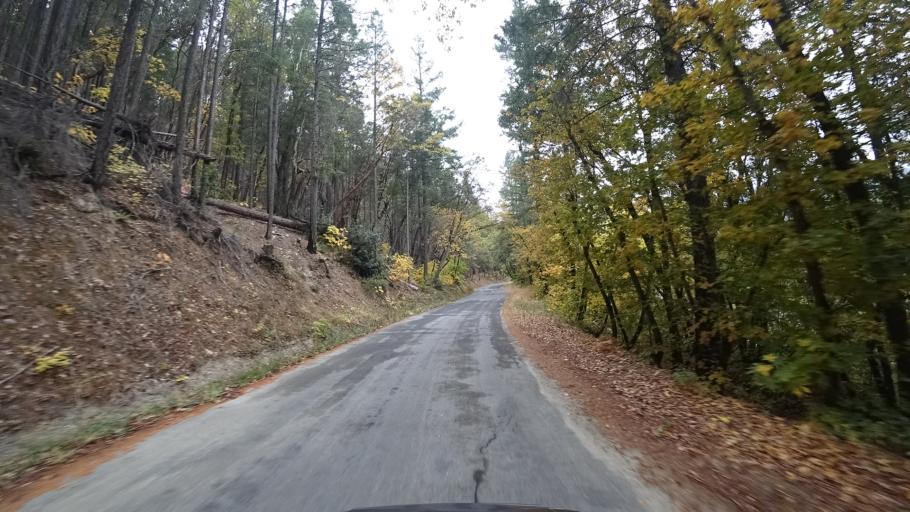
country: US
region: California
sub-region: Siskiyou County
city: Happy Camp
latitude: 41.8257
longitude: -123.1881
